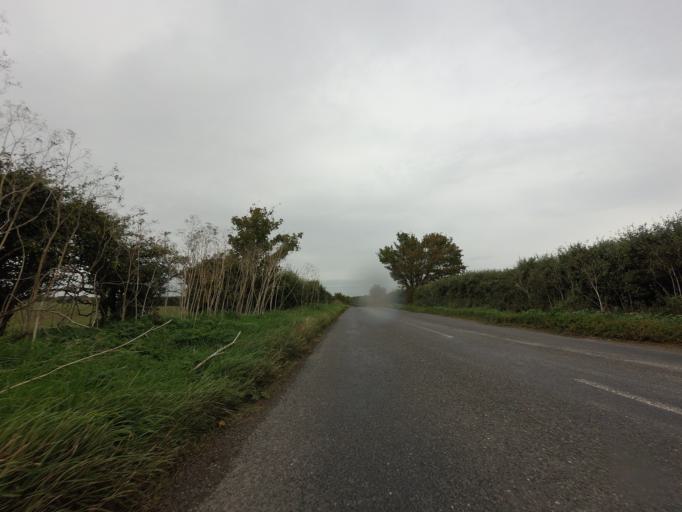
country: GB
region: England
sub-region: Cambridgeshire
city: Harston
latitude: 52.0833
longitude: 0.0788
